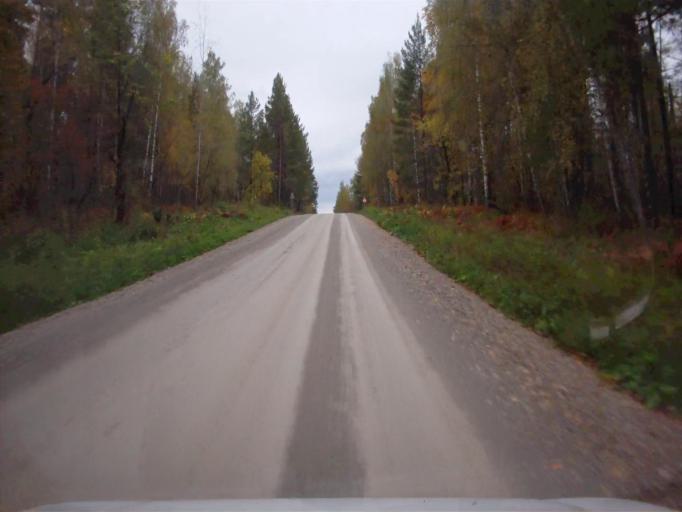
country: RU
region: Chelyabinsk
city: Nyazepetrovsk
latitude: 56.0699
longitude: 59.4316
